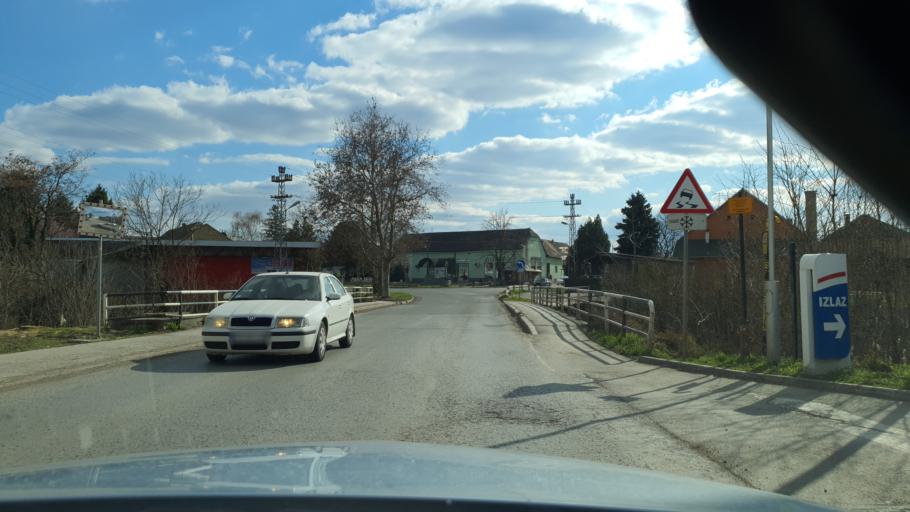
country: RS
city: Zmajevo
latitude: 45.4539
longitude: 19.6875
